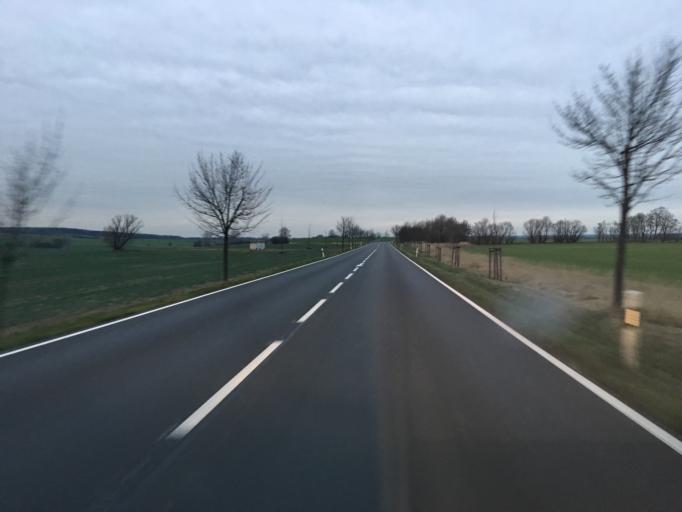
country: DE
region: Saxony
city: Oschatz
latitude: 51.3058
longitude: 13.0912
